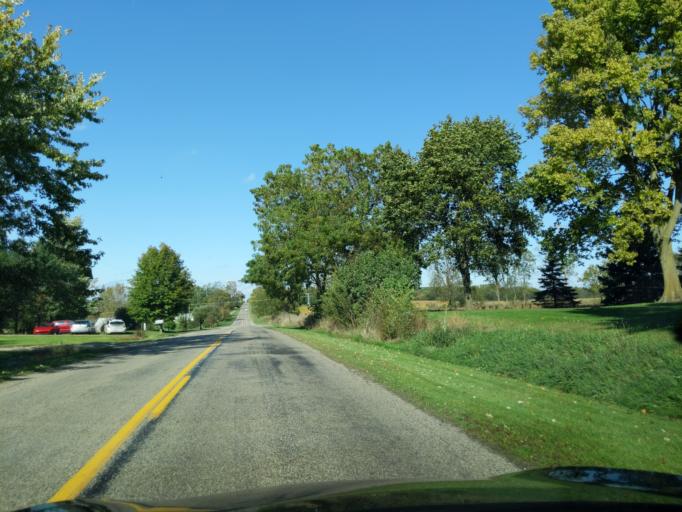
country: US
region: Michigan
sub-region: Eaton County
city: Charlotte
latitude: 42.6103
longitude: -84.7978
